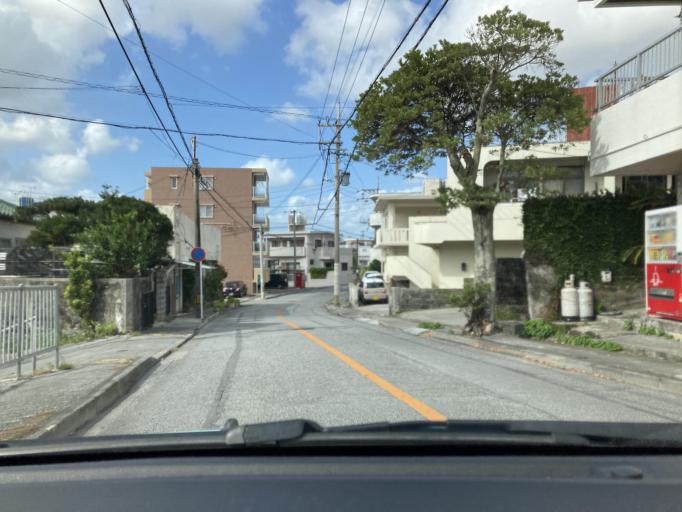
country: JP
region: Okinawa
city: Naha-shi
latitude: 26.2059
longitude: 127.7101
